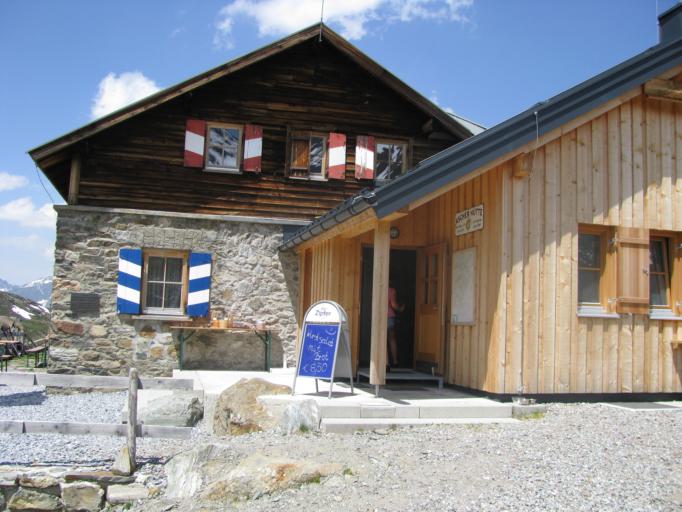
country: AT
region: Tyrol
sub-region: Politischer Bezirk Landeck
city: See
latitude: 47.0657
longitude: 10.5048
